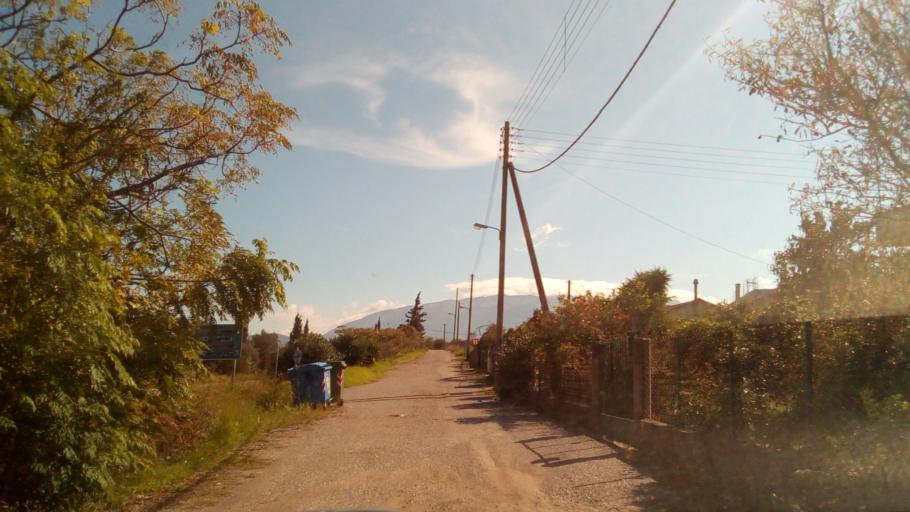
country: GR
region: West Greece
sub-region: Nomos Aitolias kai Akarnanias
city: Antirrio
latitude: 38.3434
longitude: 21.7264
